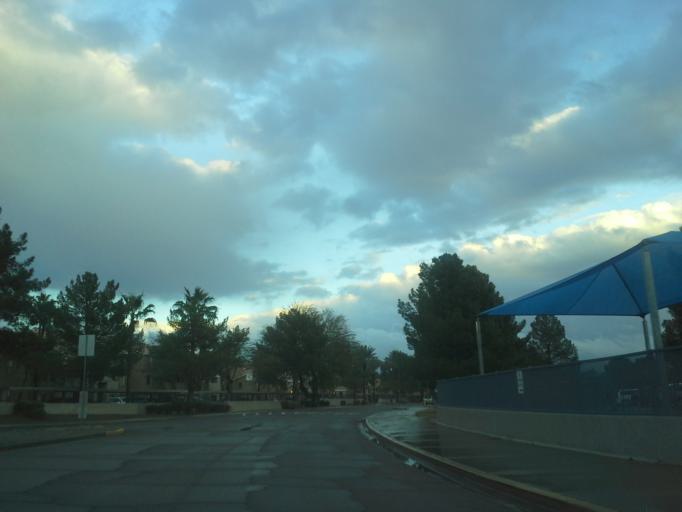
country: US
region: Arizona
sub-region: Maricopa County
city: Paradise Valley
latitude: 33.6070
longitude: -111.9906
